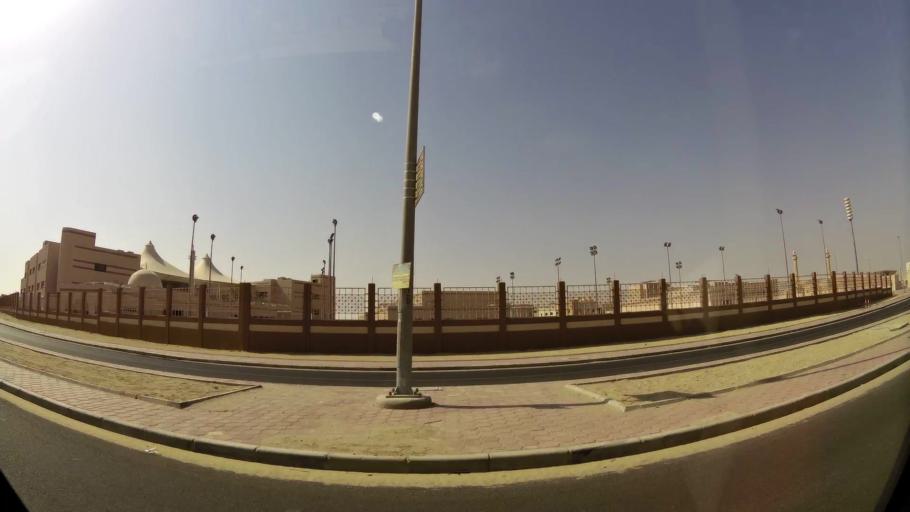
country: KW
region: Al Ahmadi
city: Al Wafrah
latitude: 28.8000
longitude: 48.0707
